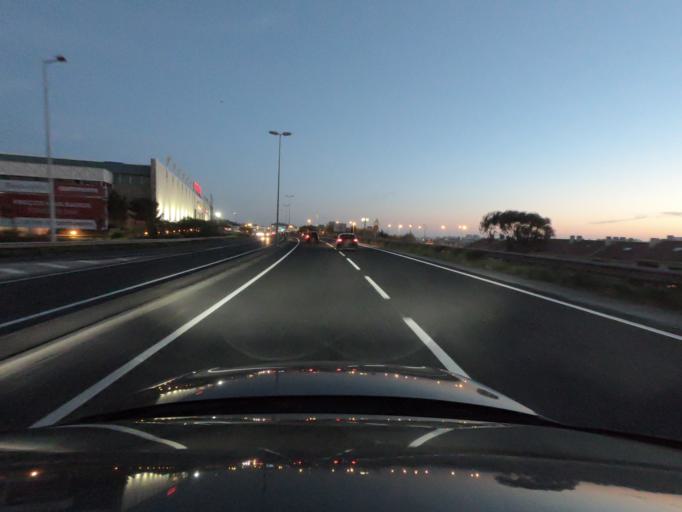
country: PT
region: Lisbon
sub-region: Oeiras
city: Porto Salvo
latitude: 38.7071
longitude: -9.3024
